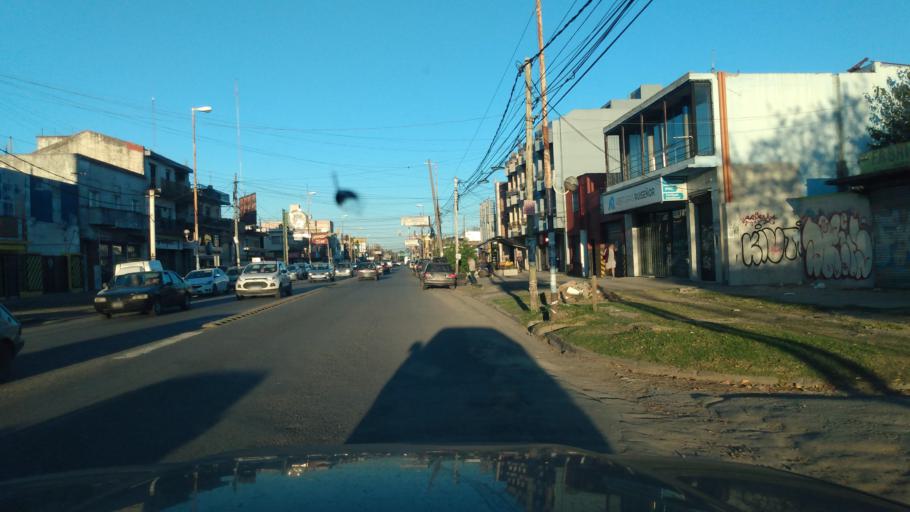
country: AR
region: Buenos Aires
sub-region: Partido de Merlo
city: Merlo
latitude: -34.6564
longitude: -58.7639
